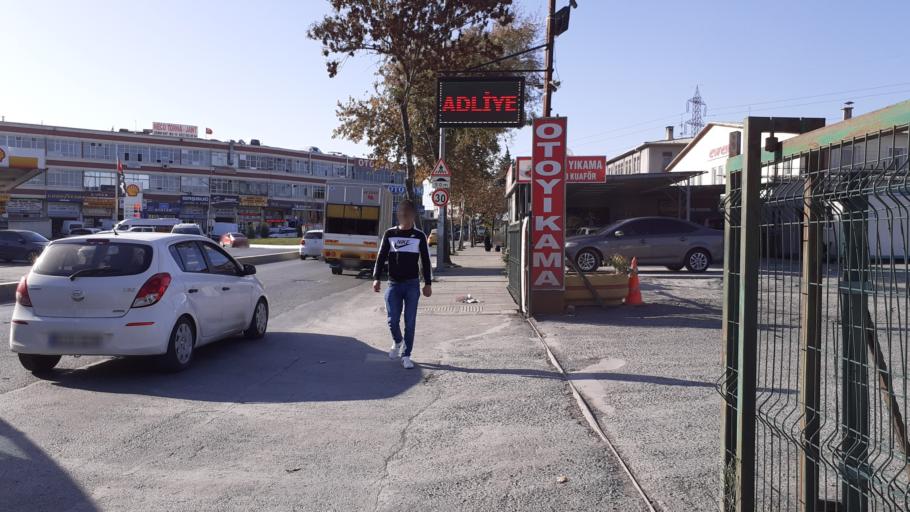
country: TR
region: Istanbul
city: Mahmutbey
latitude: 41.0103
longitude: 28.7950
